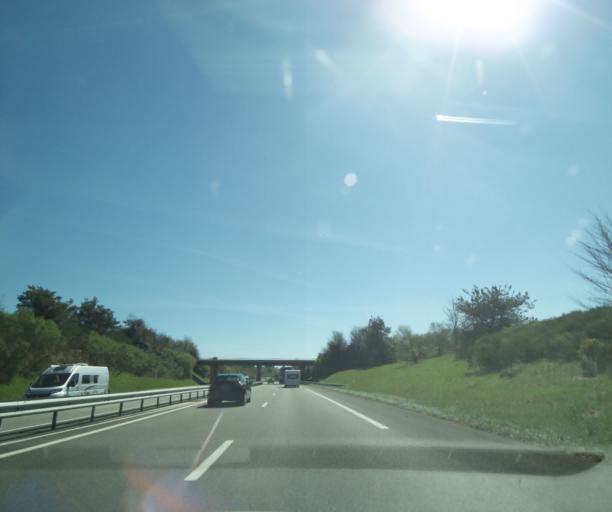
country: FR
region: Limousin
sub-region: Departement de la Haute-Vienne
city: Saint-Germain-les-Belles
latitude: 45.5281
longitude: 1.5130
